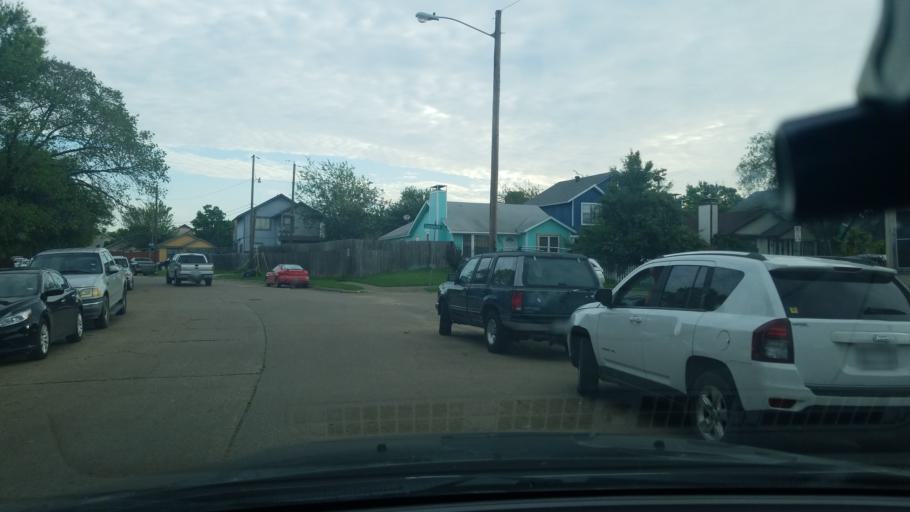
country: US
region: Texas
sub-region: Dallas County
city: Balch Springs
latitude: 32.7464
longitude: -96.6466
